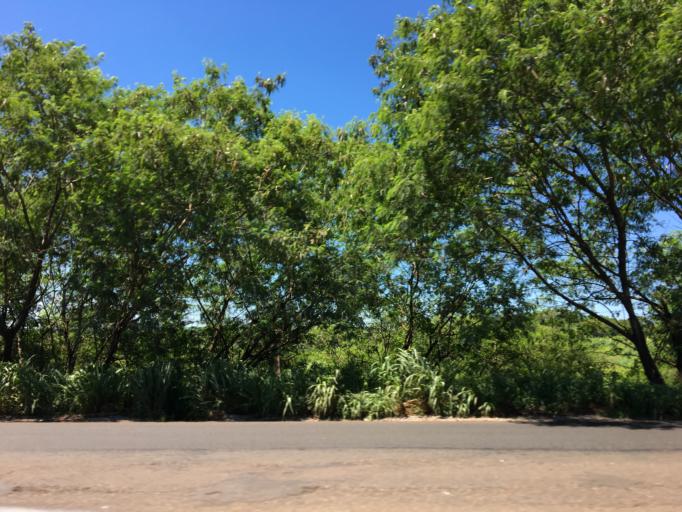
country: BR
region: Parana
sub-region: Maringa
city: Maringa
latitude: -23.4549
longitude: -51.9712
